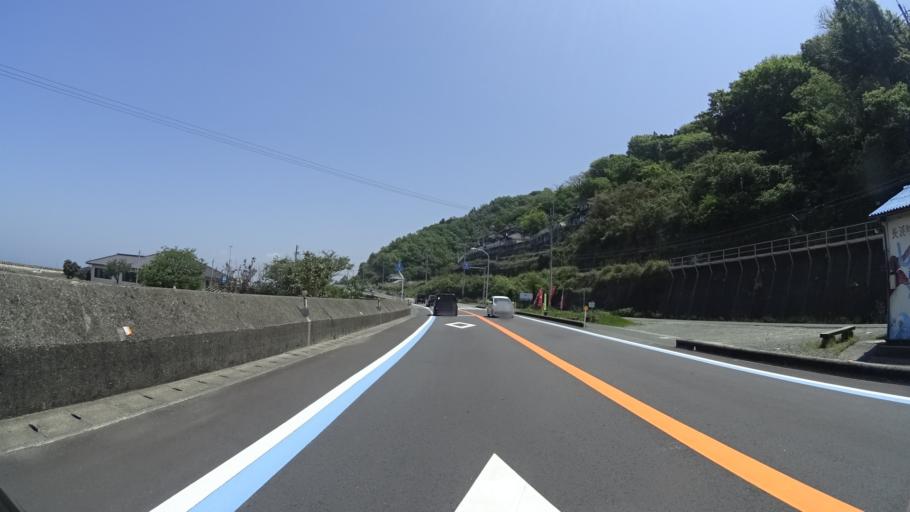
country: JP
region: Ehime
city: Ozu
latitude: 33.6339
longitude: 132.5245
